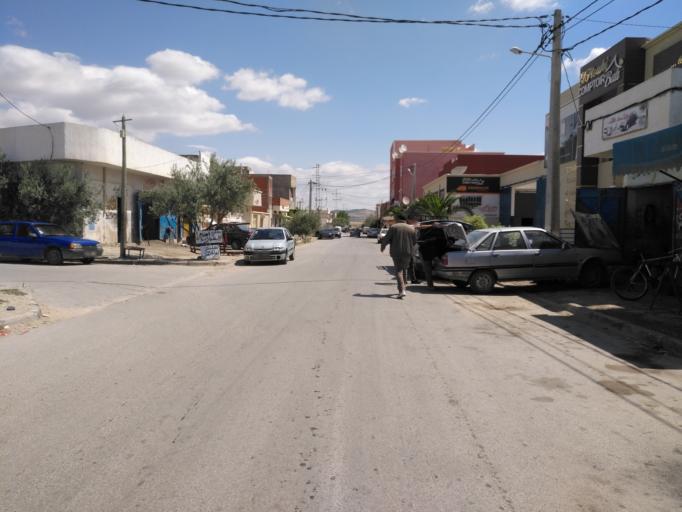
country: TN
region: Silyanah
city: Siliana
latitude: 36.0891
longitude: 9.3750
